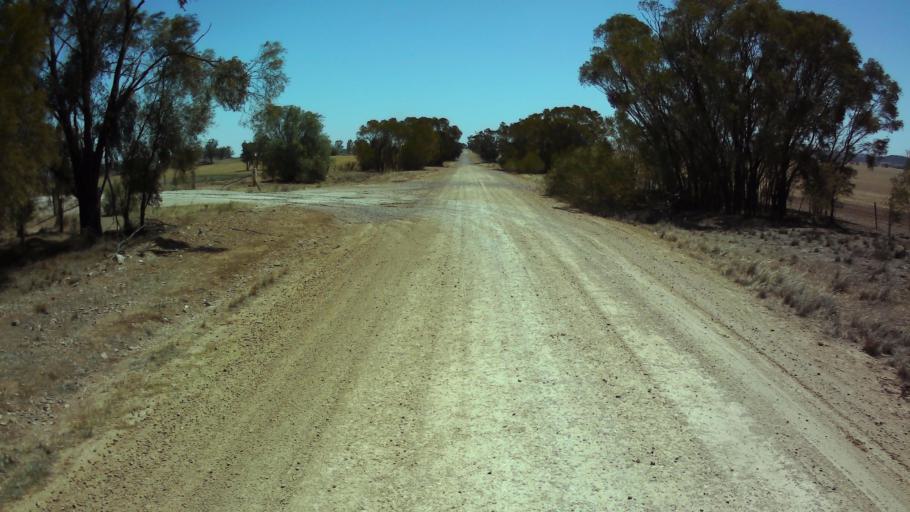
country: AU
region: New South Wales
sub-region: Forbes
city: Forbes
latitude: -33.7030
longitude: 147.7063
